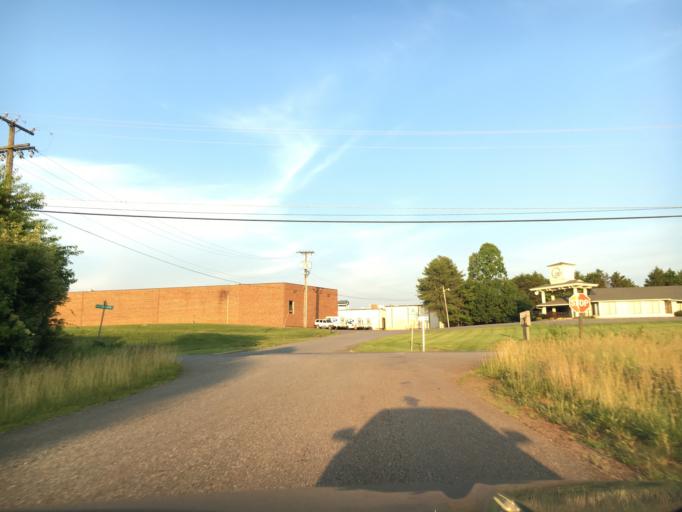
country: US
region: Virginia
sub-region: Bedford County
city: Forest
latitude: 37.3658
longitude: -79.2988
